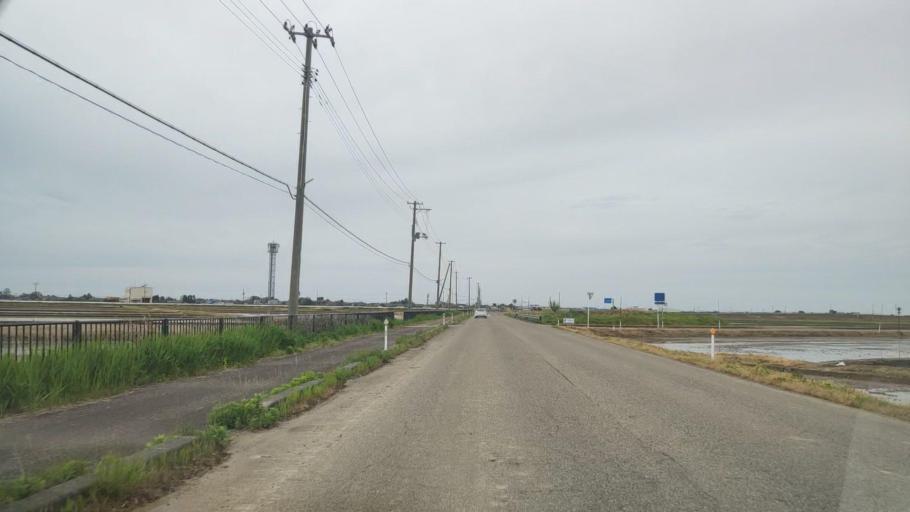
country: JP
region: Niigata
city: Shirone
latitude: 37.7352
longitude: 139.0810
